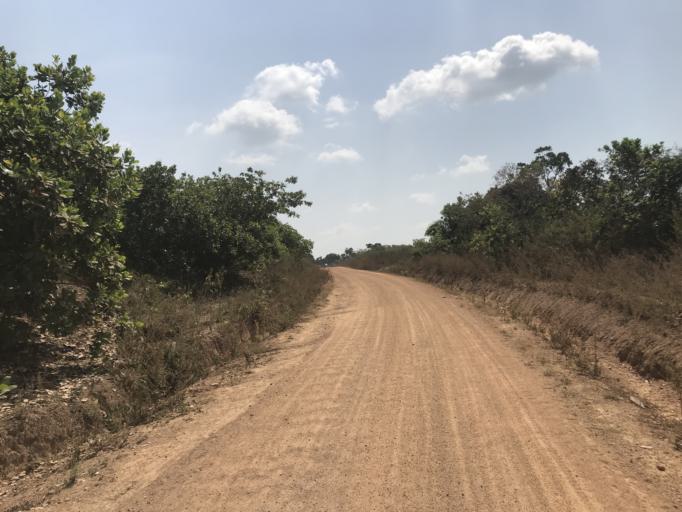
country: NG
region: Osun
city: Ifon
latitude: 7.9269
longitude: 4.4818
